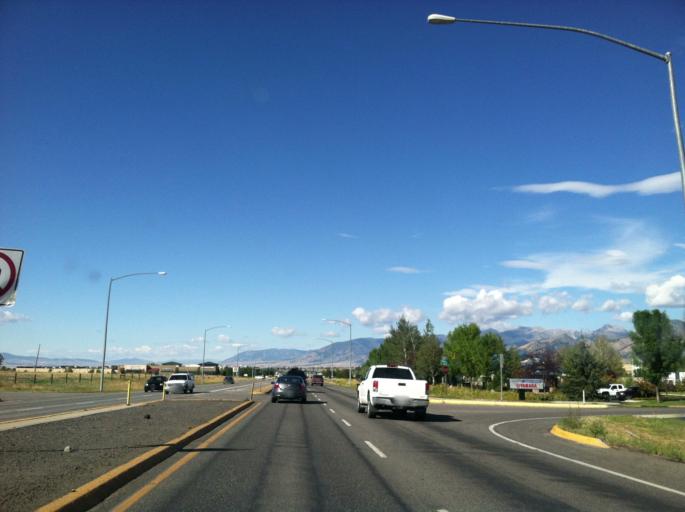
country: US
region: Montana
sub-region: Gallatin County
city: Bozeman
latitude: 45.7036
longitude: -111.0658
